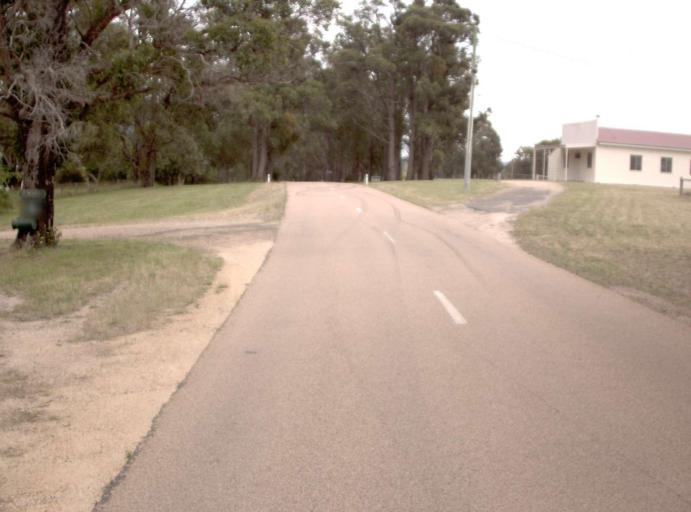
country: AU
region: Victoria
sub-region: East Gippsland
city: Bairnsdale
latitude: -37.7357
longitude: 147.5947
